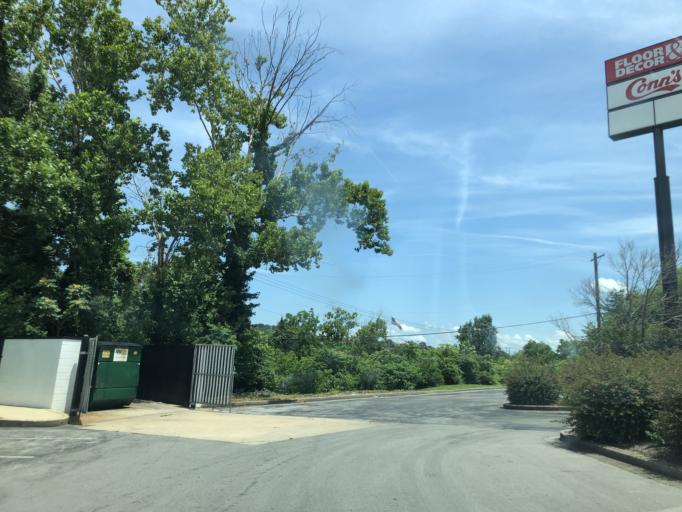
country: US
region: Tennessee
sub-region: Rutherford County
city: La Vergne
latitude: 36.0436
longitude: -86.6585
